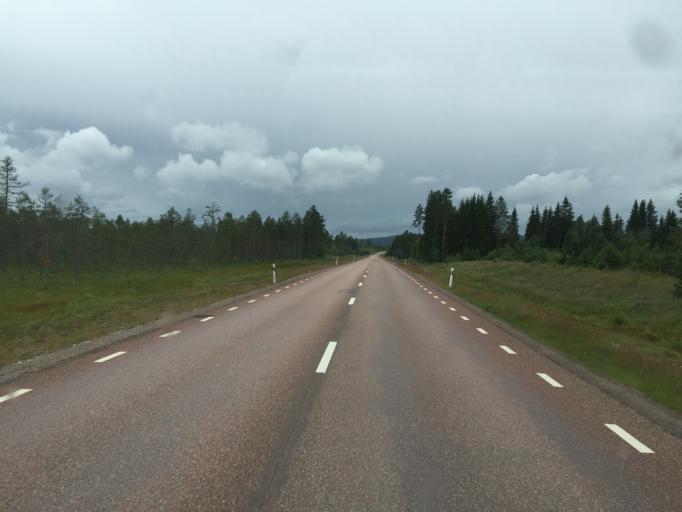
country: SE
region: Dalarna
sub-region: Malung-Saelens kommun
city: Malung
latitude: 60.6582
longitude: 13.6933
